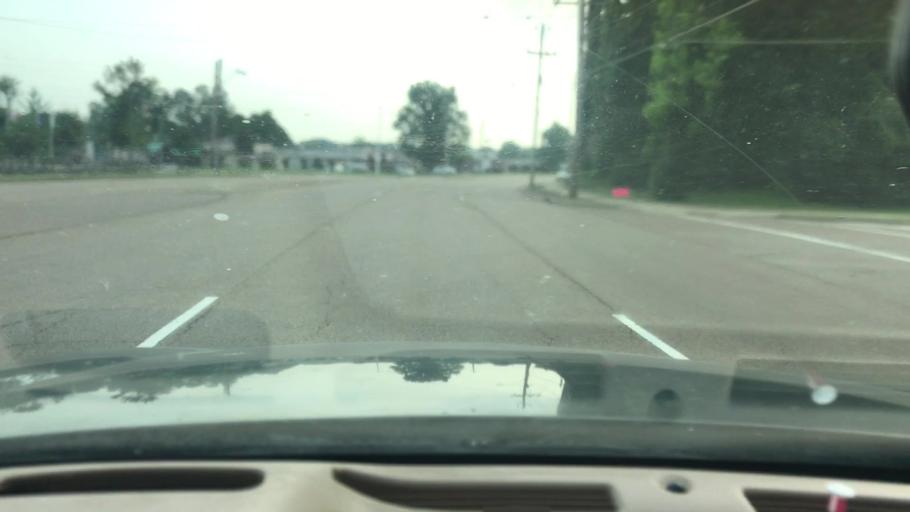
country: US
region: Tennessee
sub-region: Shelby County
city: Bartlett
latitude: 35.1992
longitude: -89.8686
